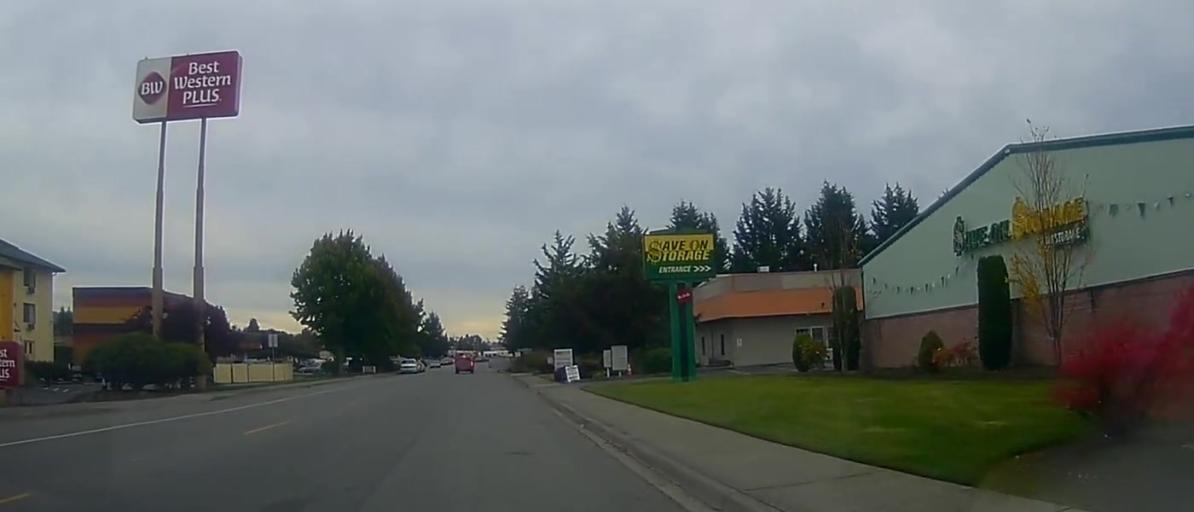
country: US
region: Washington
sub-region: Skagit County
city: Mount Vernon
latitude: 48.4425
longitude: -122.3375
